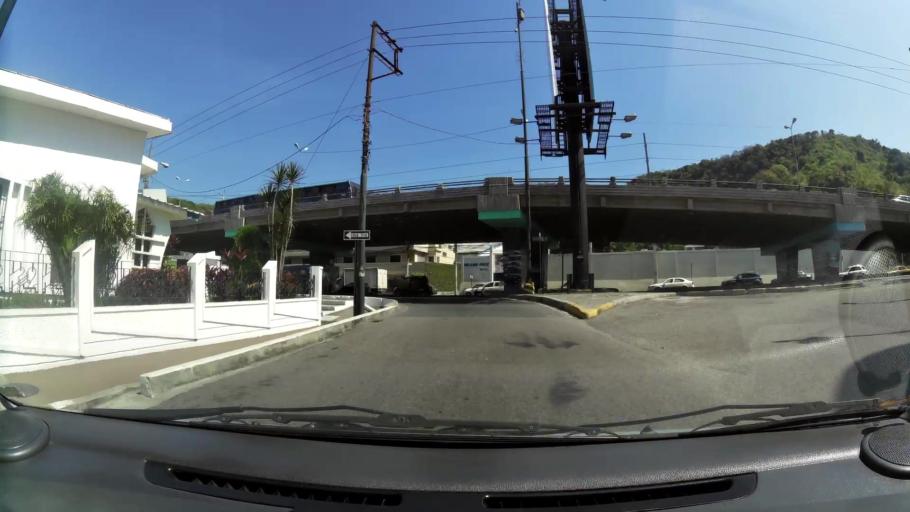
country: EC
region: Guayas
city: Guayaquil
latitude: -2.1665
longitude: -79.9216
